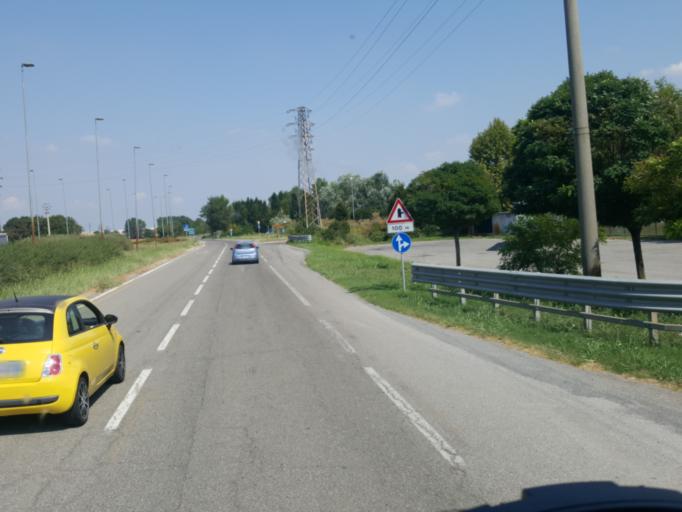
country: IT
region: Emilia-Romagna
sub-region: Provincia di Piacenza
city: Caorso
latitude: 45.0709
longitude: 9.8952
